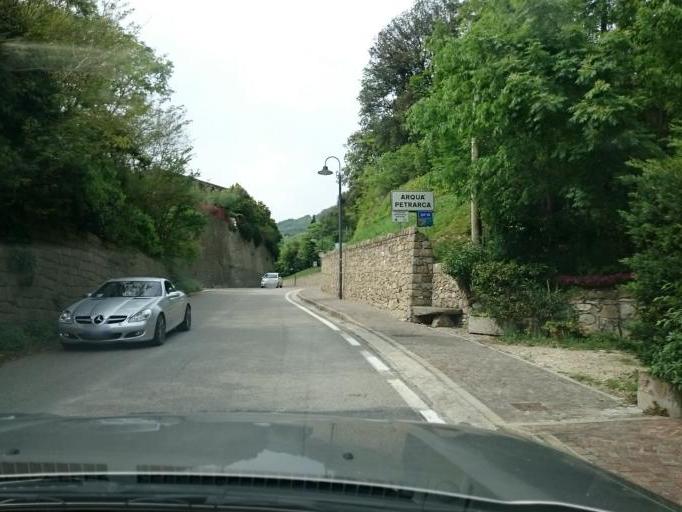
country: IT
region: Veneto
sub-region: Provincia di Padova
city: Arqua Petrarca
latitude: 45.2691
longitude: 11.7273
